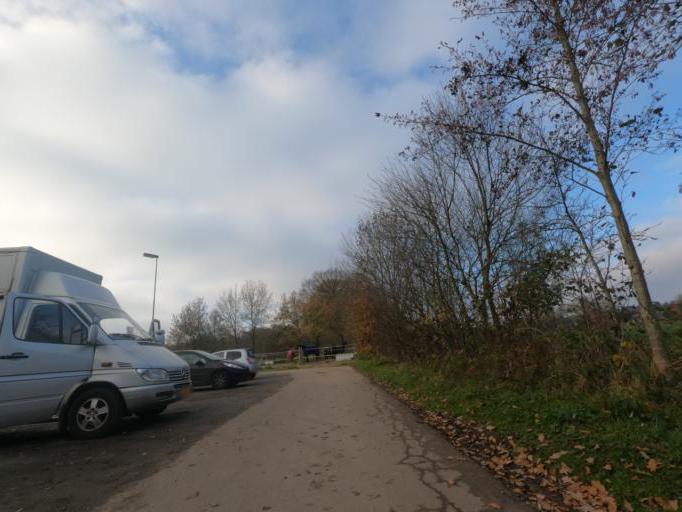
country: NL
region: Utrecht
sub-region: Gemeente Woudenberg
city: Woudenberg
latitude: 52.0850
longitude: 5.3913
